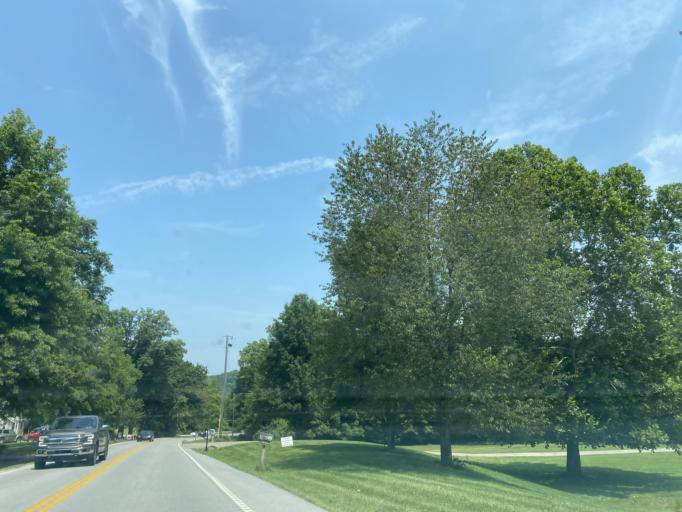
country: US
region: Kentucky
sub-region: Kenton County
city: Ryland Heights
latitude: 38.9236
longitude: -84.4400
